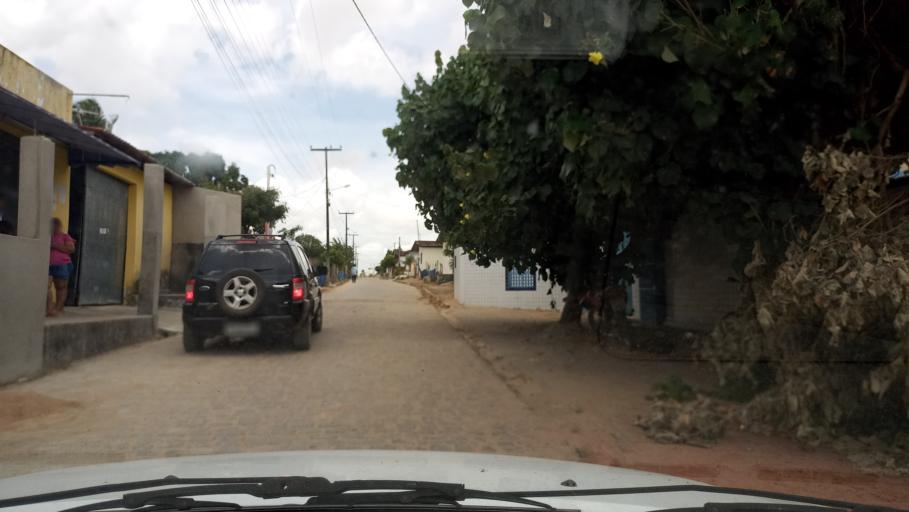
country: BR
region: Rio Grande do Norte
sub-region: Goianinha
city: Goianinha
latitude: -6.2910
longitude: -35.2814
